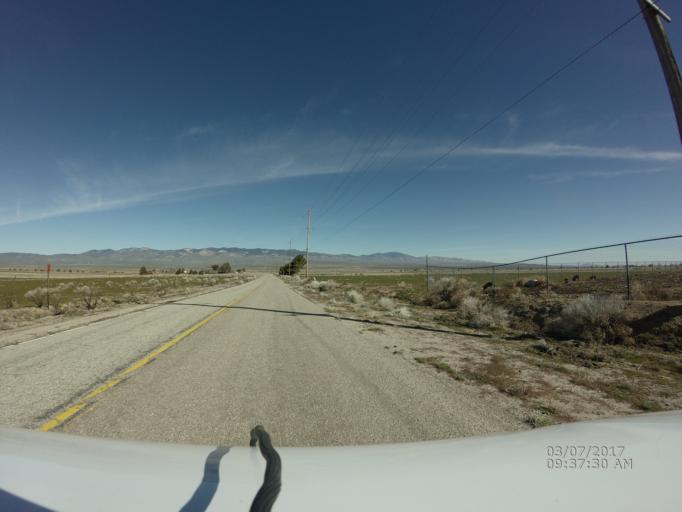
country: US
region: California
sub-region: Los Angeles County
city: Green Valley
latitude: 34.7785
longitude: -118.6070
